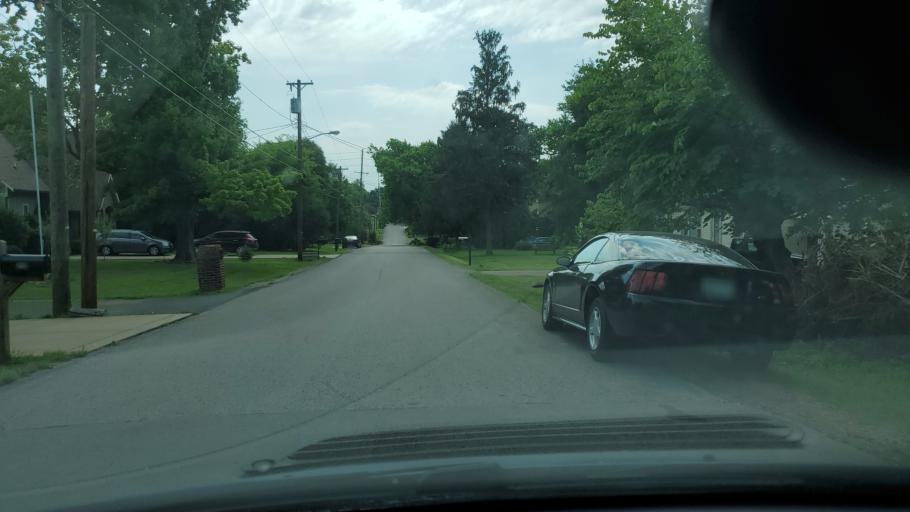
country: US
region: Tennessee
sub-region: Davidson County
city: Nashville
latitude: 36.2304
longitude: -86.7288
